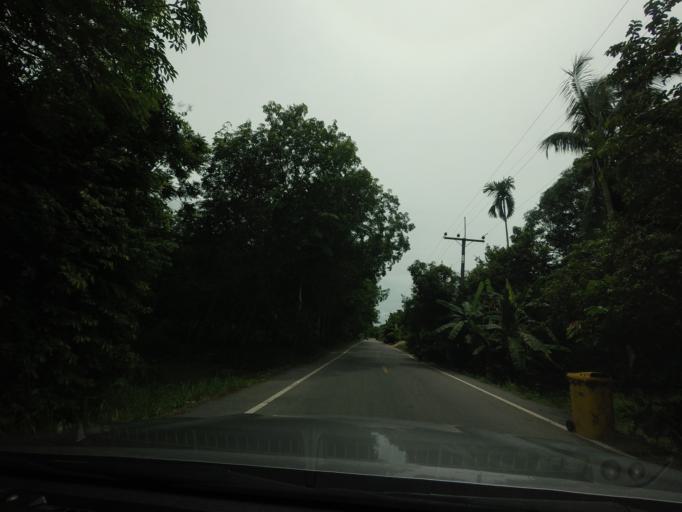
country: TH
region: Pattani
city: Kapho
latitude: 6.6209
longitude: 101.5436
